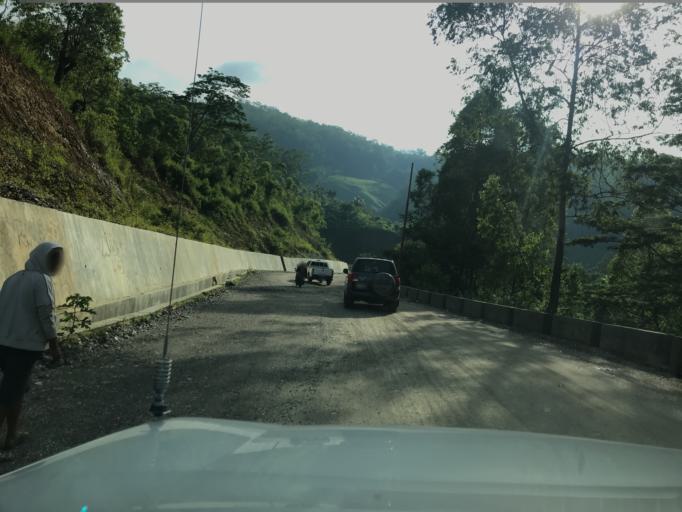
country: TL
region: Aileu
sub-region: Aileu Villa
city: Aileu
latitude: -8.6590
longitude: 125.5292
